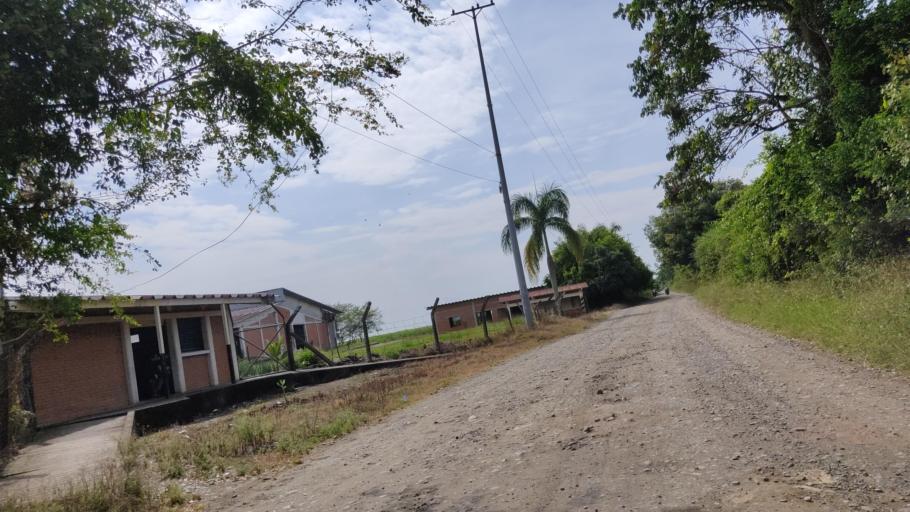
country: CO
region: Cauca
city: Buenos Aires
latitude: 3.1273
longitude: -76.5887
